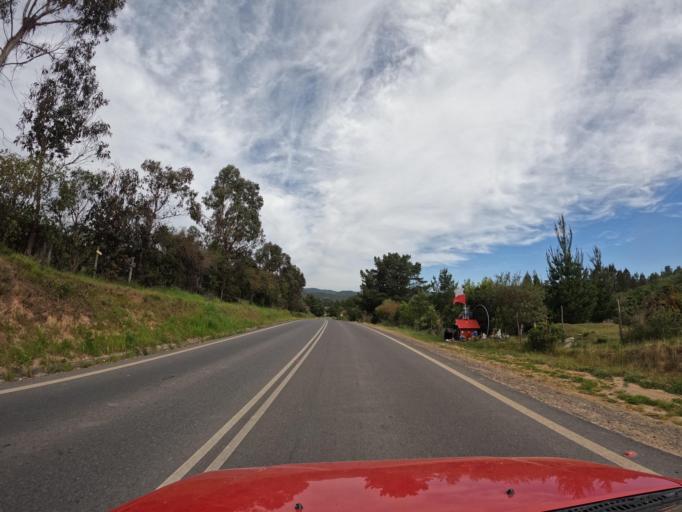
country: CL
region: Maule
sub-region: Provincia de Talca
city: Talca
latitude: -35.3299
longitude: -71.9282
